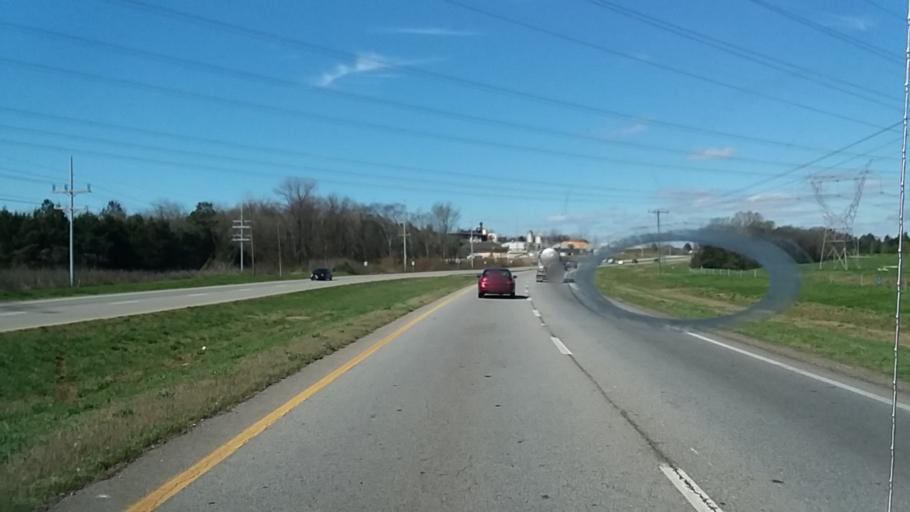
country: US
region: Alabama
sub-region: Morgan County
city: Trinity
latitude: 34.6201
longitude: -87.0728
